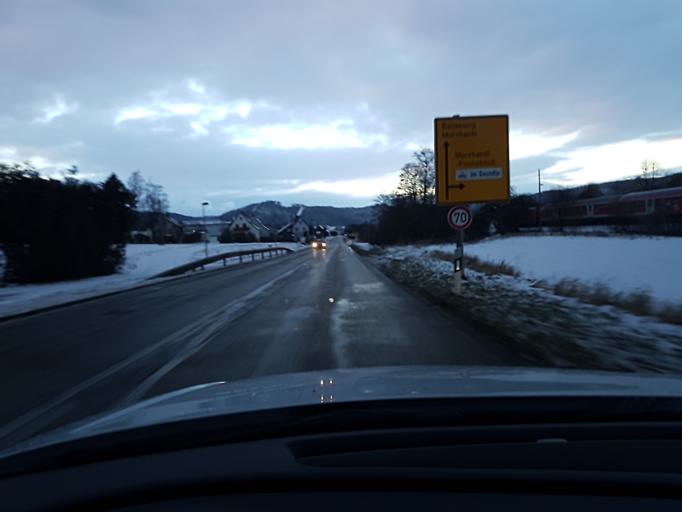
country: DE
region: Baden-Wuerttemberg
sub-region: Regierungsbezirk Stuttgart
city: Oberrot
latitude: 48.9780
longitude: 9.6576
